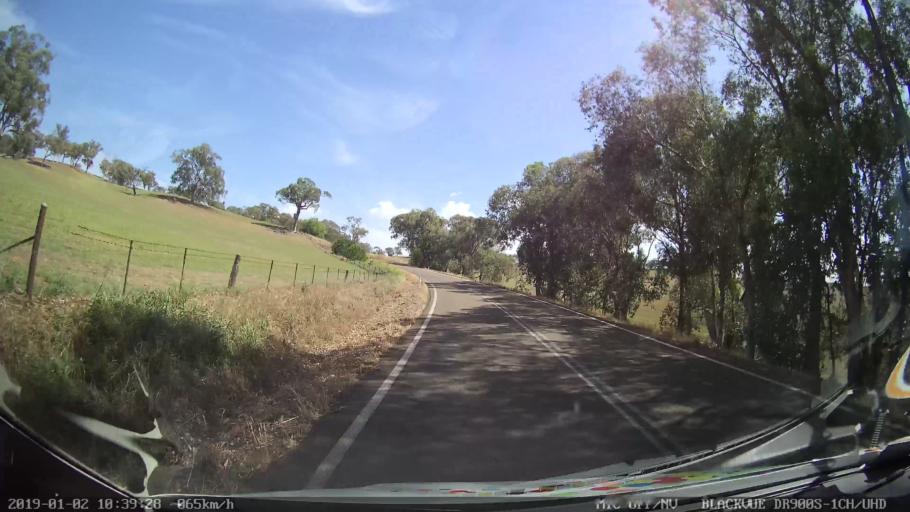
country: AU
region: New South Wales
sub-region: Gundagai
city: Gundagai
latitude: -34.8105
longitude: 148.3191
